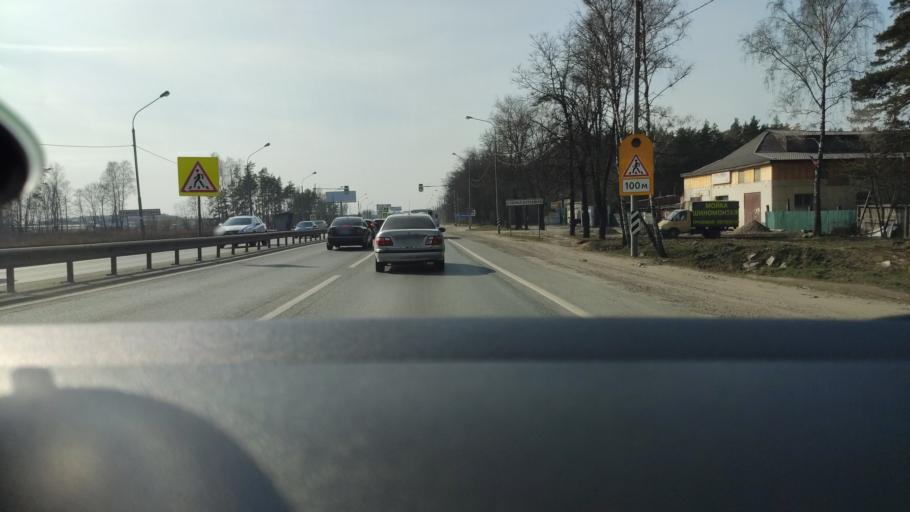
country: RU
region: Moskovskaya
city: Staraya Kupavna
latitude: 55.8224
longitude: 38.1852
